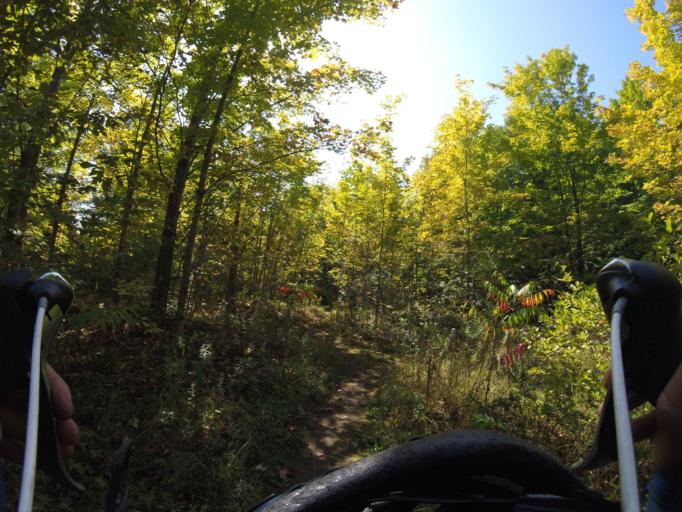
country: CA
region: Ontario
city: Bells Corners
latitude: 45.3006
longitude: -75.8896
